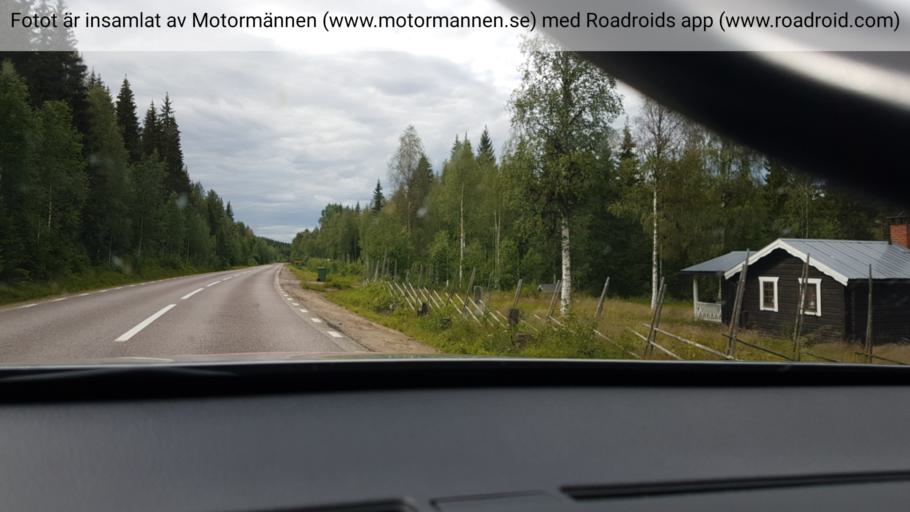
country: NO
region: Hedmark
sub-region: Trysil
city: Innbygda
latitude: 60.9007
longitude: 12.5750
